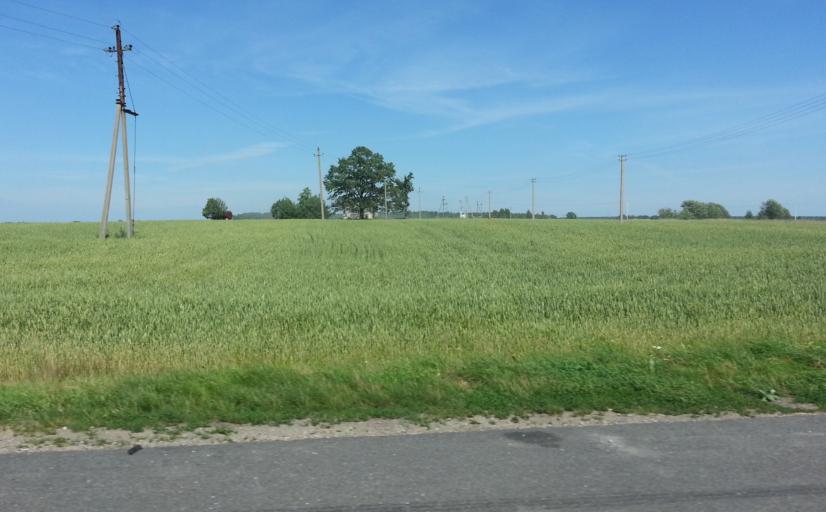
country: LT
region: Panevezys
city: Pasvalys
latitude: 56.1709
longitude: 24.4446
